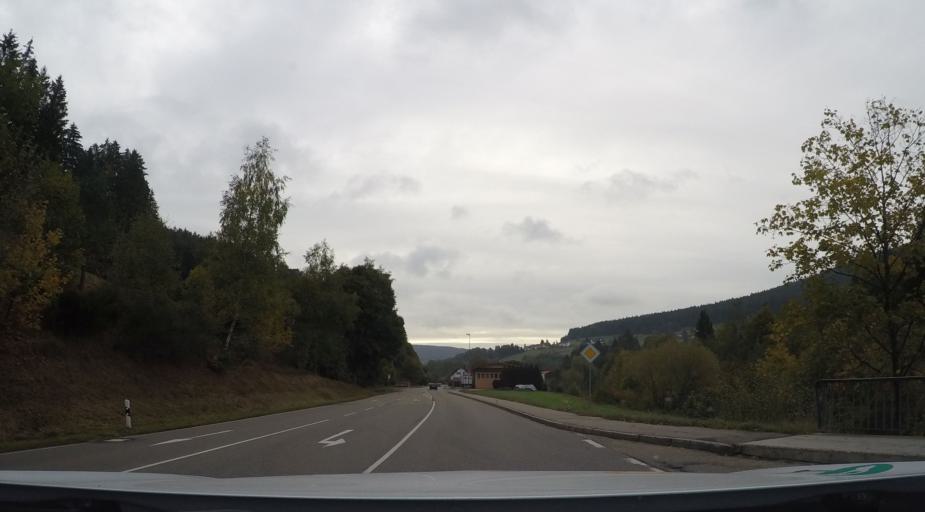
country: DE
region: Baden-Wuerttemberg
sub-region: Karlsruhe Region
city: Baiersbronn
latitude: 48.5181
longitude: 8.3360
